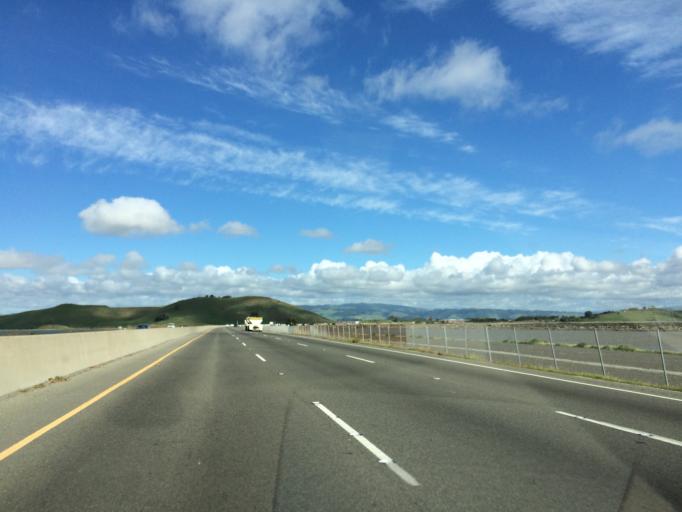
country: US
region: California
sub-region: Alameda County
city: Newark
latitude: 37.5275
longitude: -122.0963
